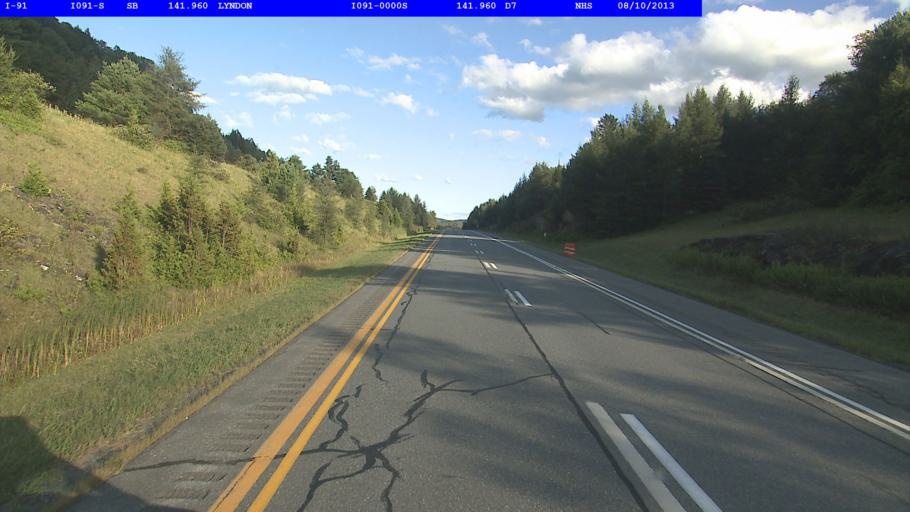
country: US
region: Vermont
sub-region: Caledonia County
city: Lyndonville
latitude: 44.5768
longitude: -72.0488
